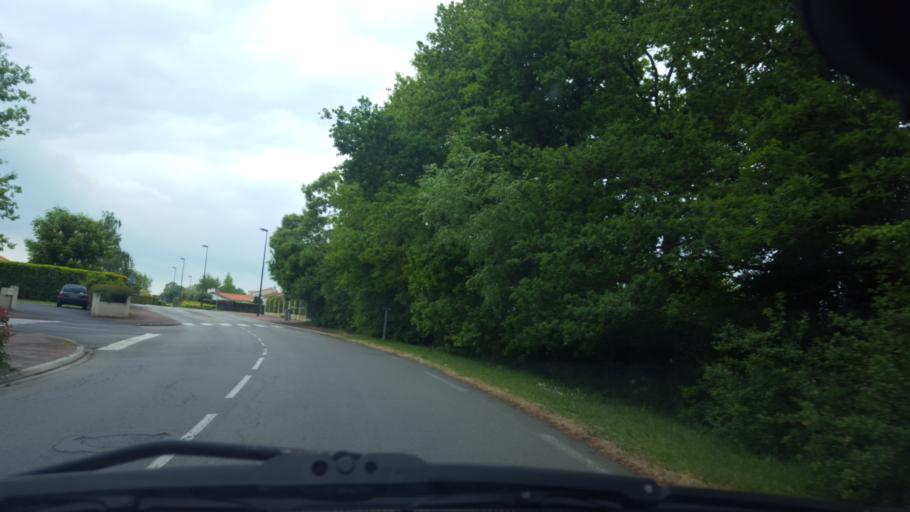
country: FR
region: Pays de la Loire
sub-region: Departement de la Loire-Atlantique
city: La Limouziniere
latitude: 46.9962
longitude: -1.5979
